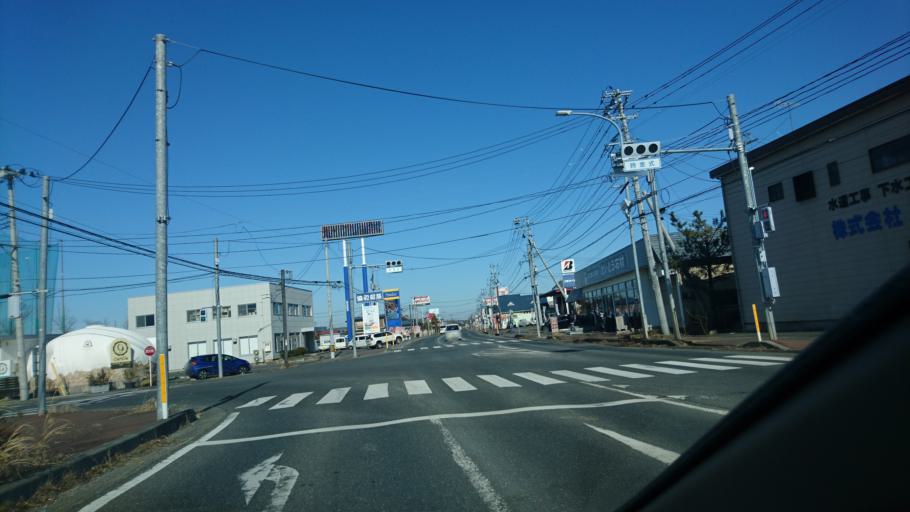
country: JP
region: Miyagi
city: Furukawa
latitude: 38.5981
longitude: 140.9767
